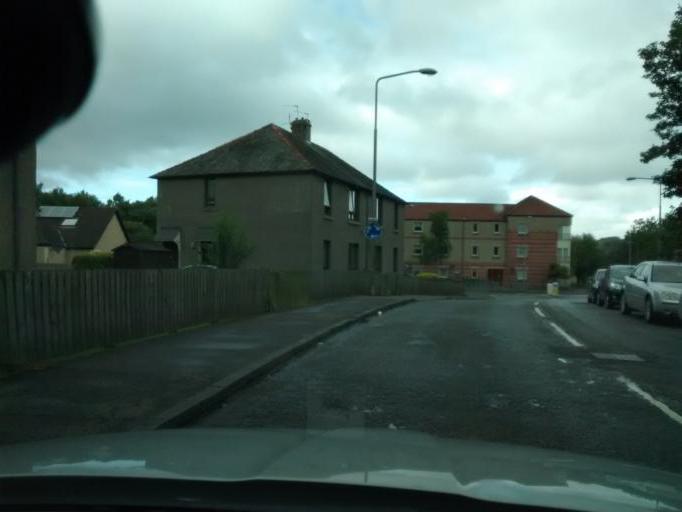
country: GB
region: Scotland
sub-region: West Lothian
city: Bathgate
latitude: 55.9043
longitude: -3.6482
